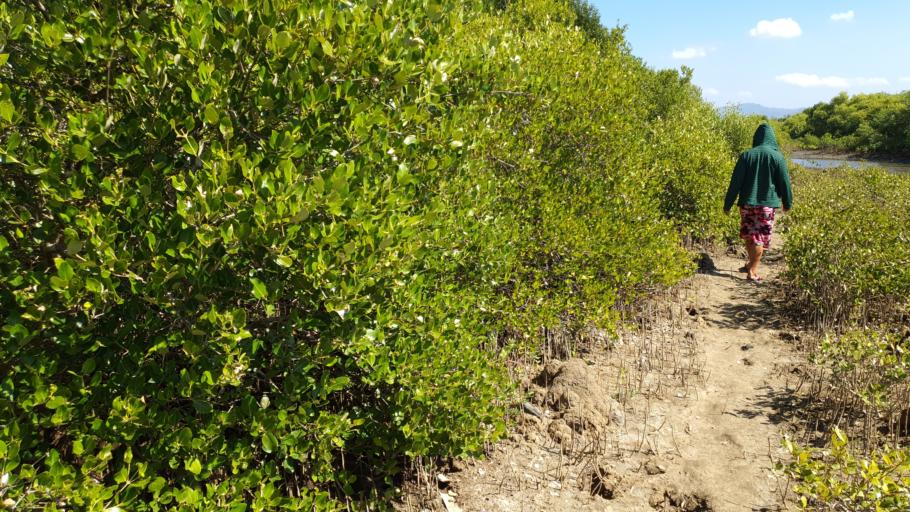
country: PH
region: Ilocos
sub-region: Province of La Union
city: Payocpoc Sur
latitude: 16.5025
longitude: 120.3068
